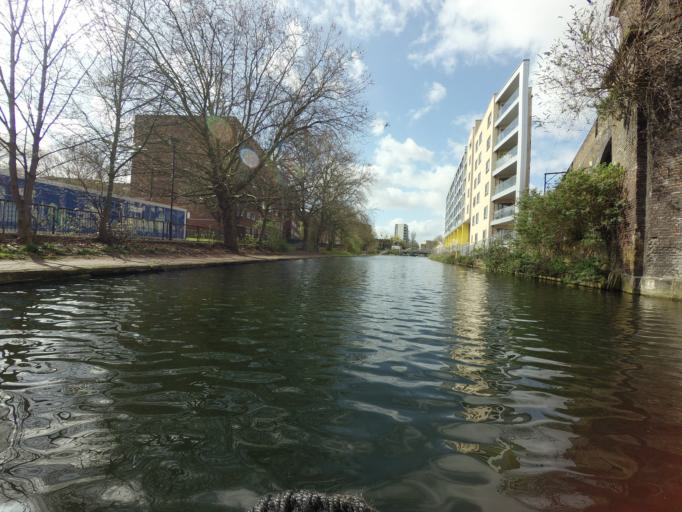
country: GB
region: England
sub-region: Greater London
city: Poplar
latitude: 51.5162
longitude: -0.0337
